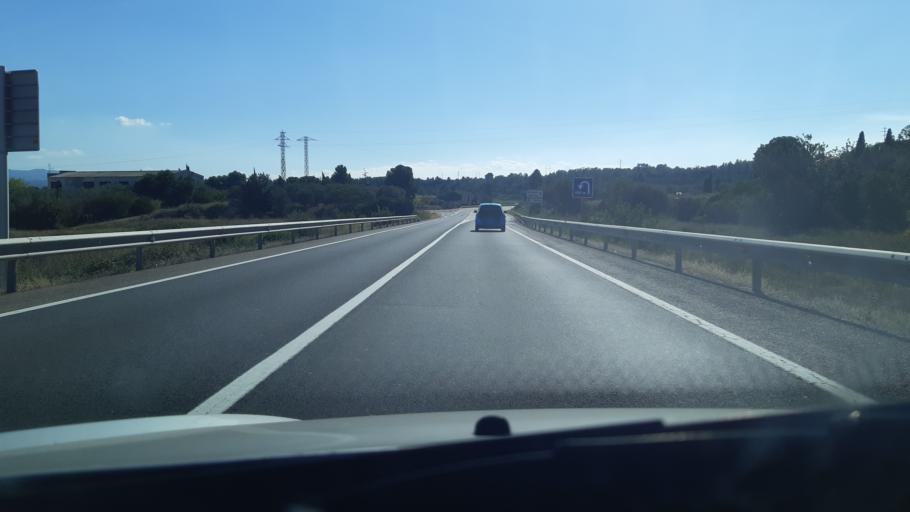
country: ES
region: Catalonia
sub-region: Provincia de Tarragona
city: Tivenys
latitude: 40.9067
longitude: 0.4832
